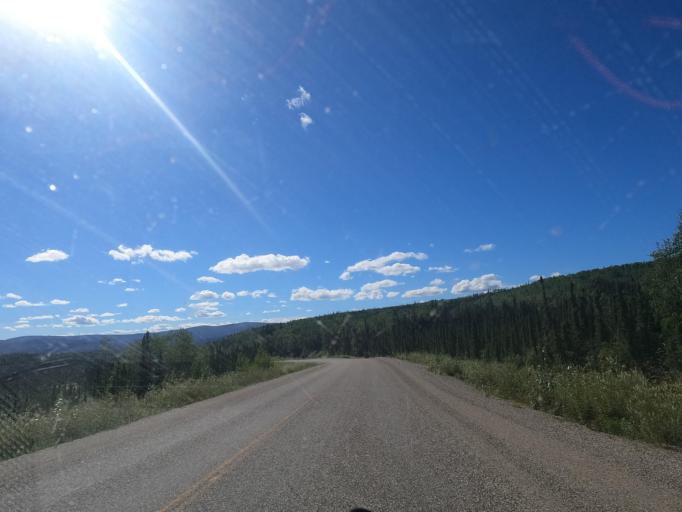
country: CA
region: Yukon
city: Dawson City
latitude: 63.9392
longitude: -138.4798
